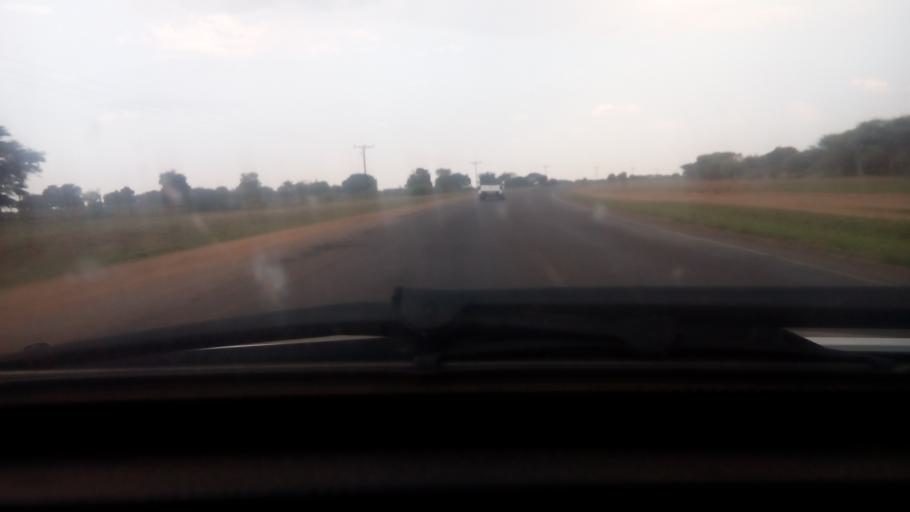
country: BW
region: Kweneng
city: Metsemotlhaba
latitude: -24.4781
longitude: 25.7272
